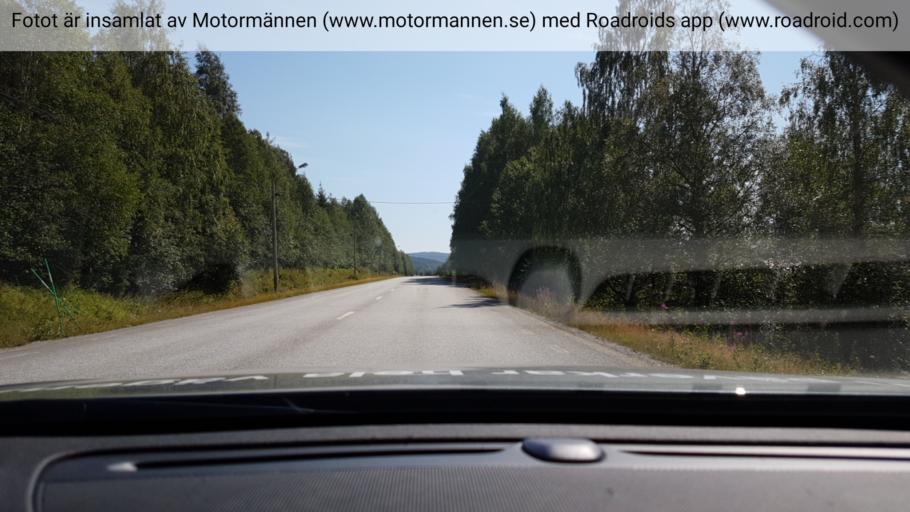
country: SE
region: Vaesterbotten
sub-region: Vannas Kommun
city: Vannasby
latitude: 64.1321
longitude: 19.9515
